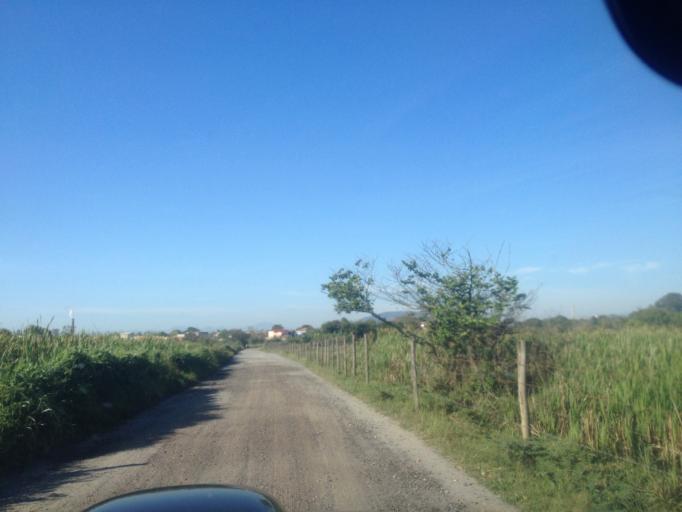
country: BR
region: Rio de Janeiro
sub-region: Porto Real
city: Porto Real
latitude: -22.4035
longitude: -44.2972
